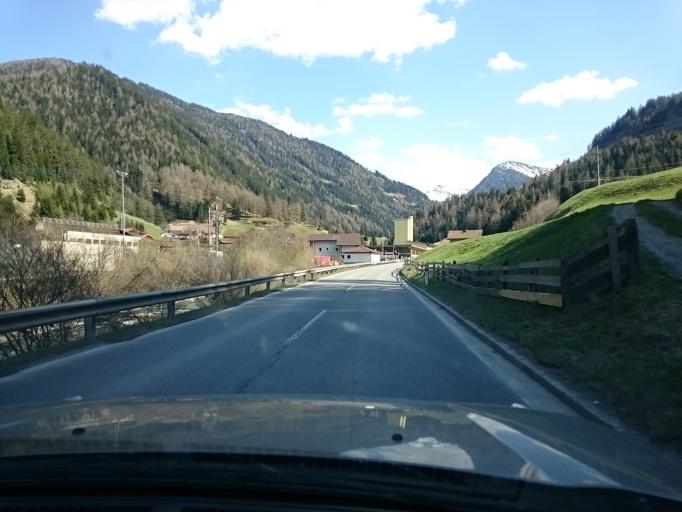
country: AT
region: Tyrol
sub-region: Politischer Bezirk Innsbruck Land
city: Steinach am Brenner
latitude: 47.0833
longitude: 11.4728
